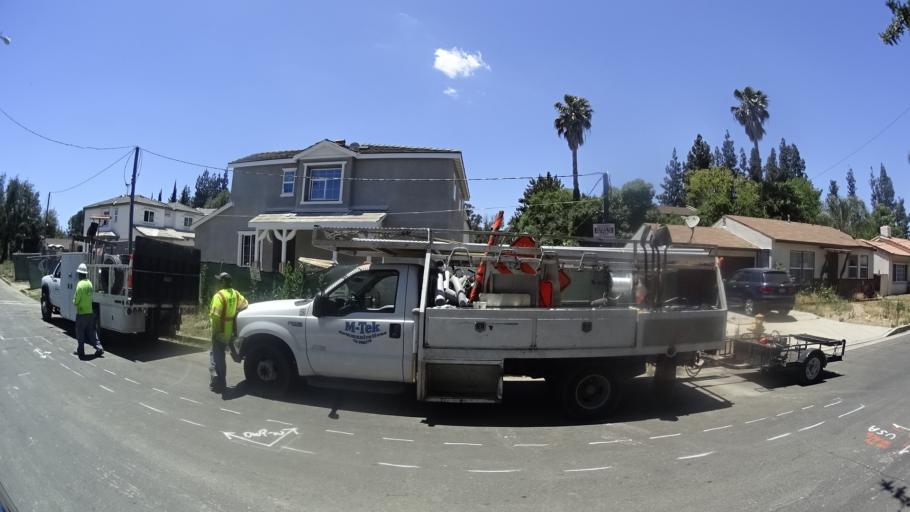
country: US
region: California
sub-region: Los Angeles County
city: Van Nuys
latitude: 34.1992
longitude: -118.4723
